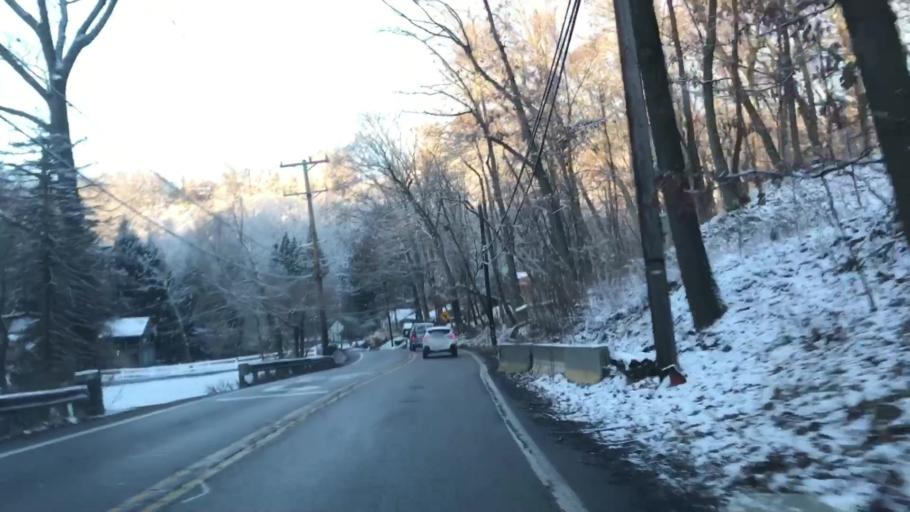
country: US
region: Pennsylvania
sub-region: Allegheny County
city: West View
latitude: 40.5441
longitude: -80.0415
